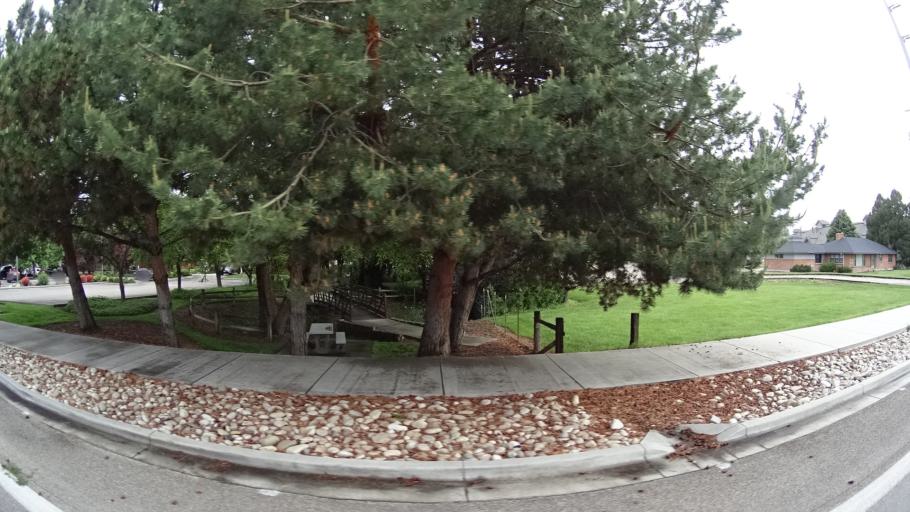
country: US
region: Idaho
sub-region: Ada County
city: Eagle
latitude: 43.6952
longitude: -116.3498
